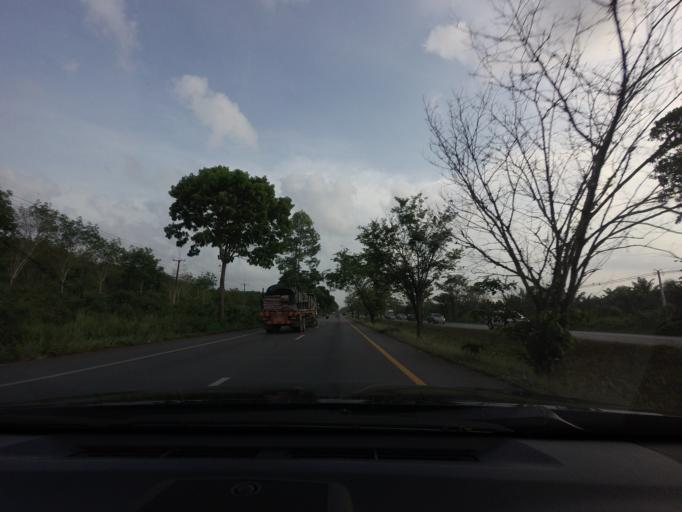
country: TH
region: Chumphon
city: Lang Suan
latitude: 9.8872
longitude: 99.0632
